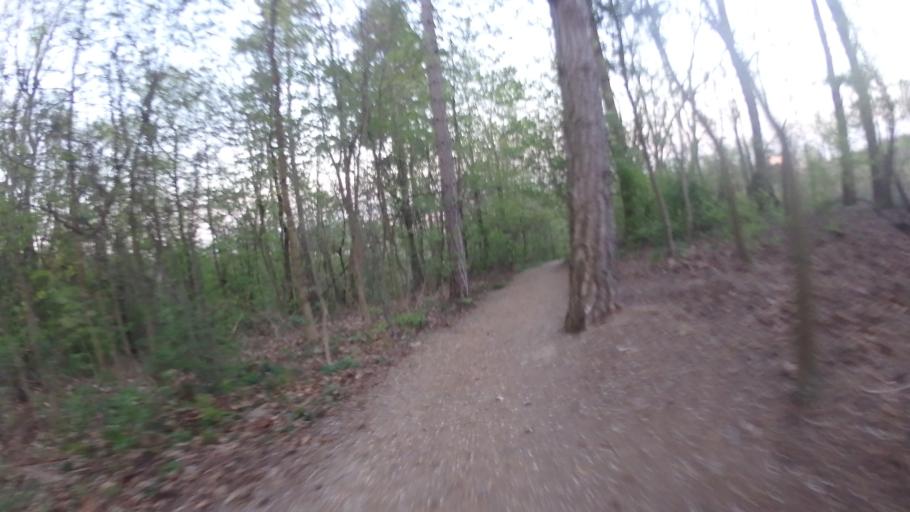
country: CZ
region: South Moravian
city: Ostopovice
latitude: 49.1819
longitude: 16.5558
